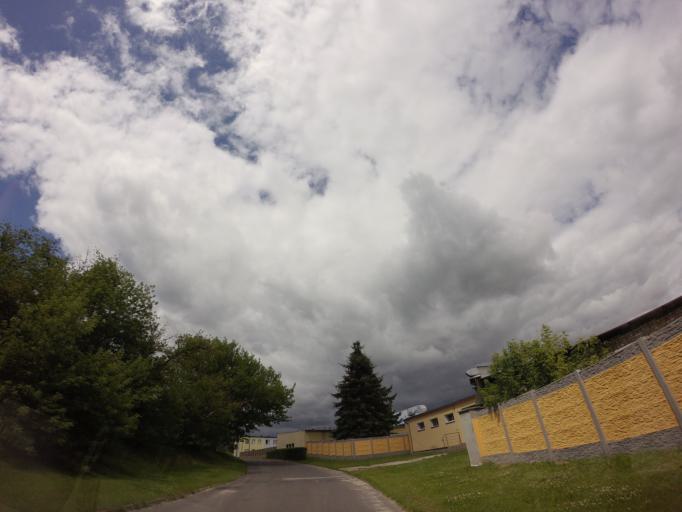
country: PL
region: West Pomeranian Voivodeship
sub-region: Powiat drawski
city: Drawsko Pomorskie
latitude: 53.4722
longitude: 15.7632
